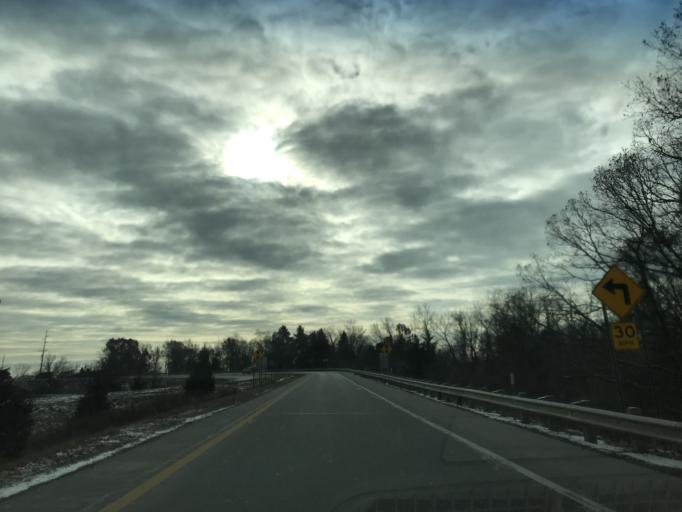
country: US
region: Michigan
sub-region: Oakland County
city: Clarkston
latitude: 42.7364
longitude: -83.3818
